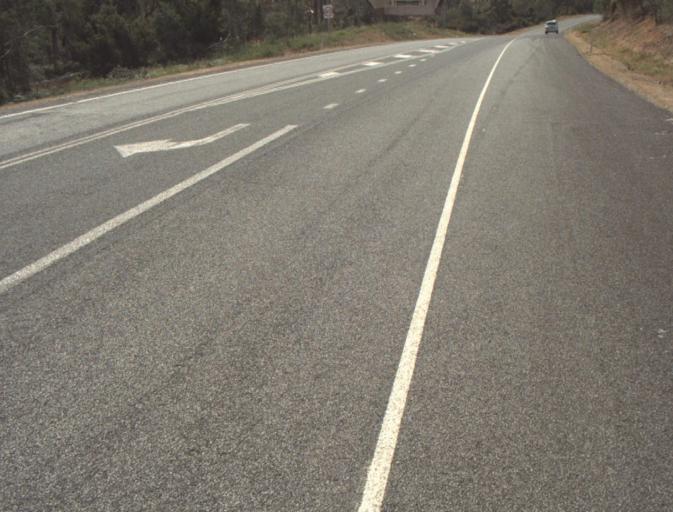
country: AU
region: Tasmania
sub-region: Launceston
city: Mayfield
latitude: -41.3060
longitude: 147.0487
